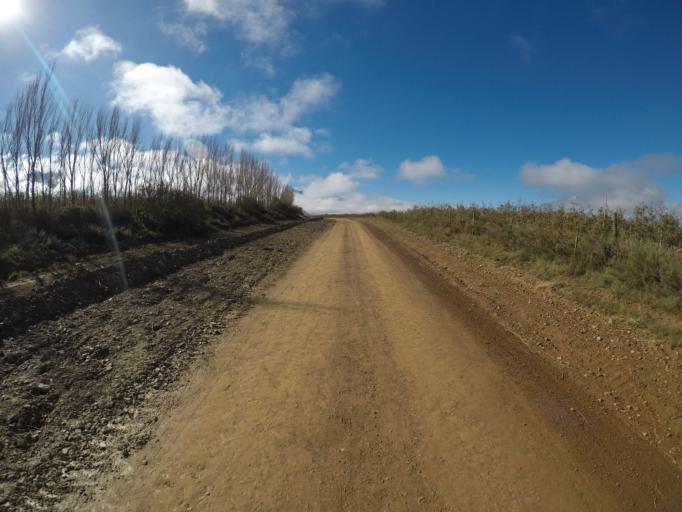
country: ZA
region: Western Cape
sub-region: Overberg District Municipality
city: Caledon
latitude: -34.1184
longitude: 19.7361
